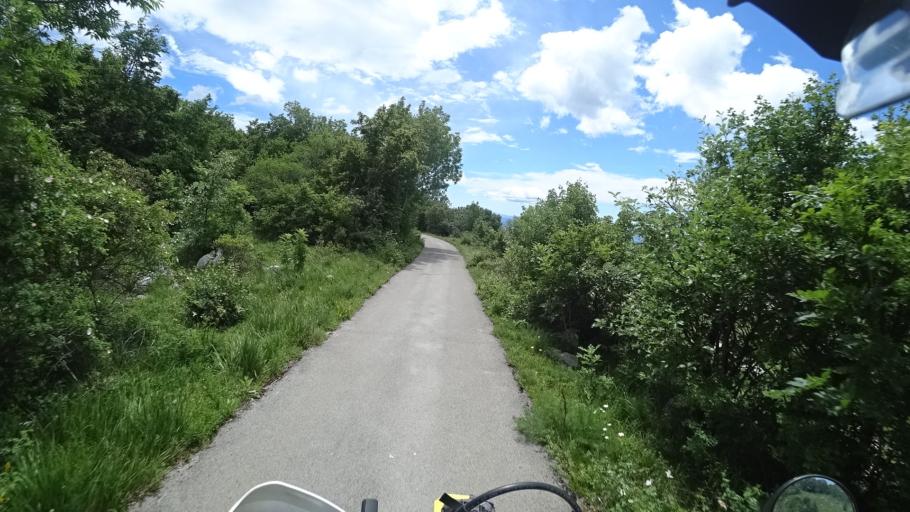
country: HR
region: Primorsko-Goranska
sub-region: Grad Crikvenica
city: Jadranovo
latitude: 45.2453
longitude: 14.6725
